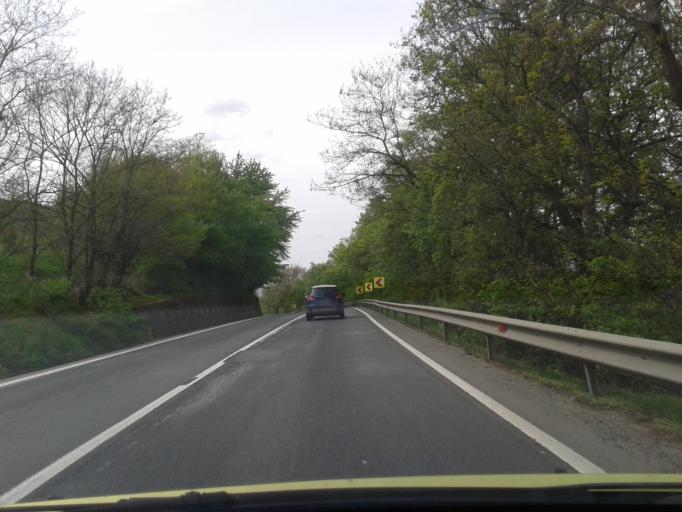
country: RO
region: Hunedoara
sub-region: Comuna Branisca
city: Branisca
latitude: 45.9186
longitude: 22.7223
